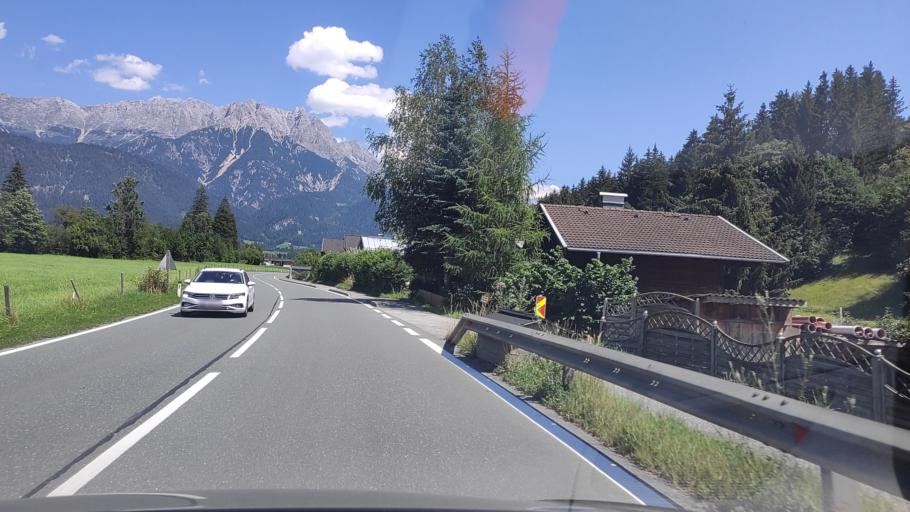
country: AT
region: Salzburg
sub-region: Politischer Bezirk Zell am See
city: Leogang
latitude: 47.4395
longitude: 12.7996
